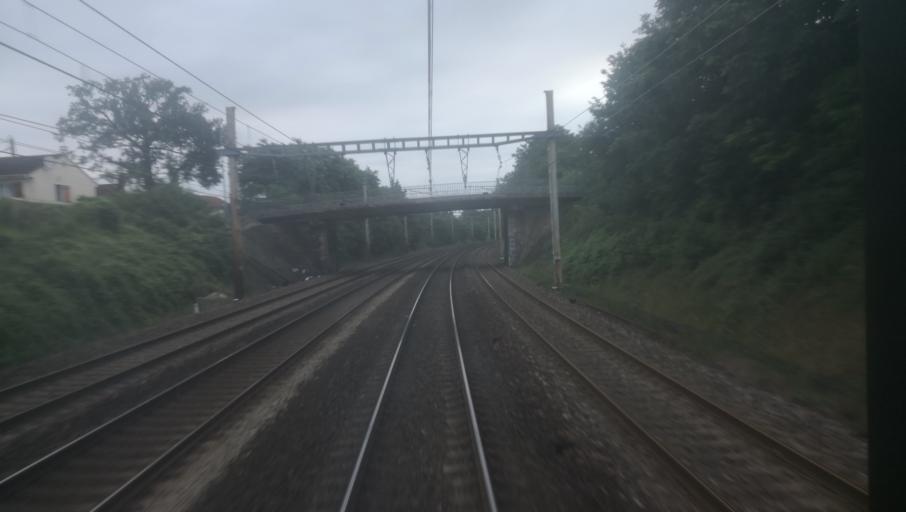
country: FR
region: Ile-de-France
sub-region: Departement de l'Essonne
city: Sainte-Genevieve-des-Bois
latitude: 48.6497
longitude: 2.3083
